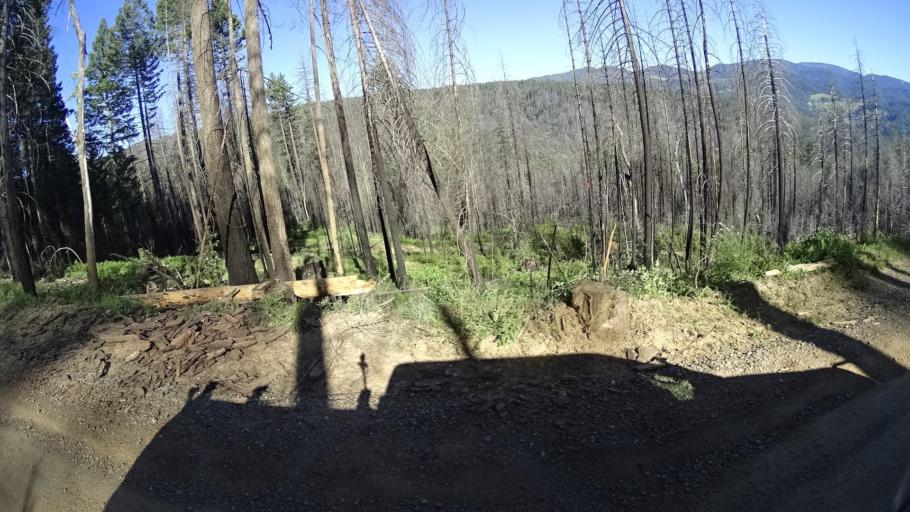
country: US
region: California
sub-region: Lake County
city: Upper Lake
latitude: 39.3776
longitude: -122.9902
